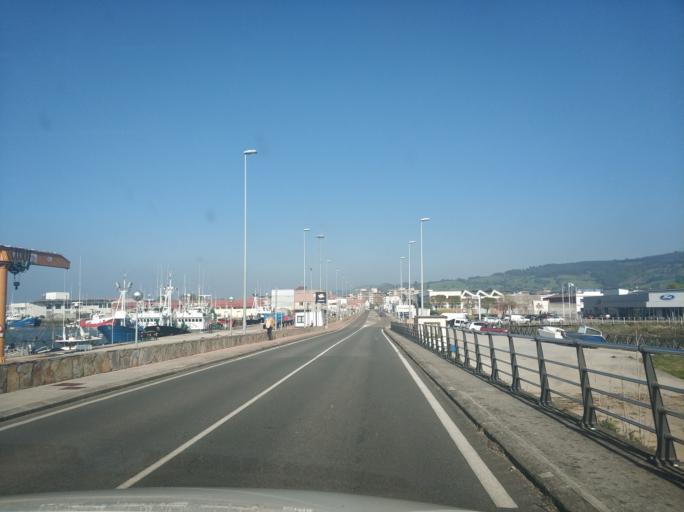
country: ES
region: Cantabria
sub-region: Provincia de Cantabria
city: Colindres
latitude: 43.3935
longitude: -3.4640
